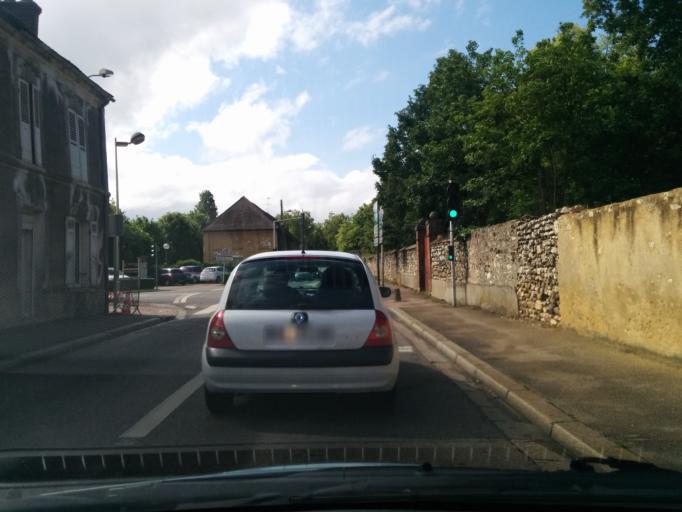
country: FR
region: Ile-de-France
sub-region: Departement des Yvelines
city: Rosny-sur-Seine
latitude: 49.0015
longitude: 1.6298
